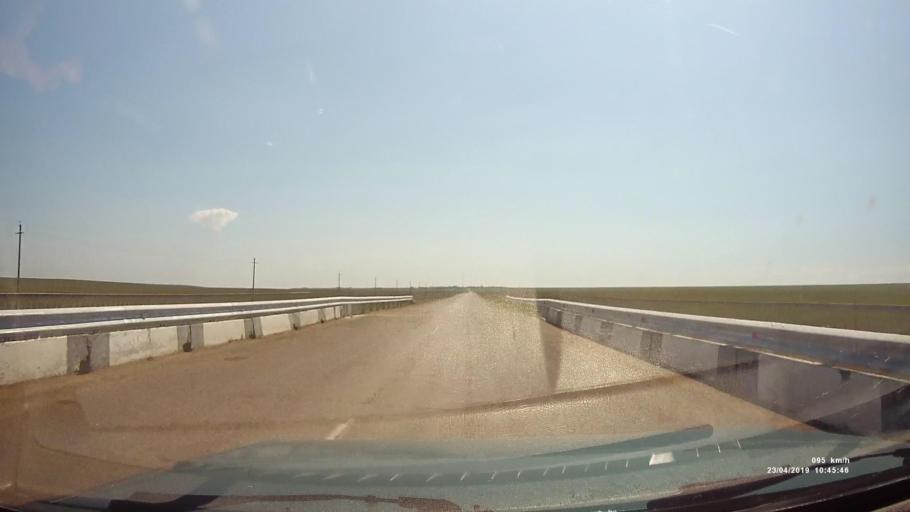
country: RU
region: Kalmykiya
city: Yashalta
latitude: 46.4486
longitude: 42.6800
